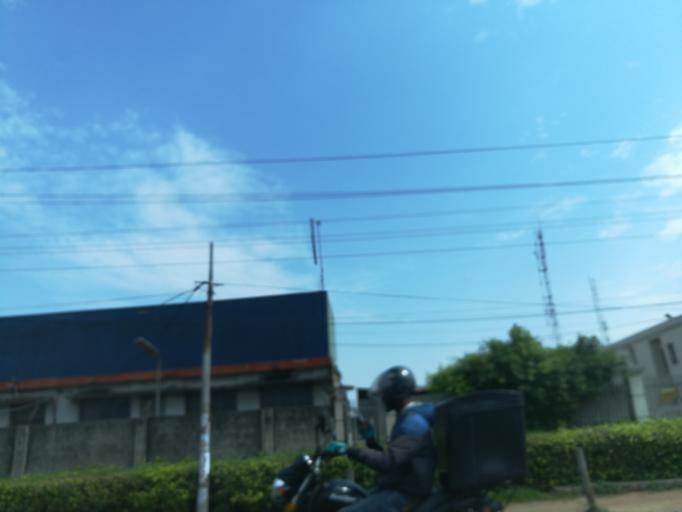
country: NG
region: Lagos
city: Oshodi
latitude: 6.5462
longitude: 3.3280
